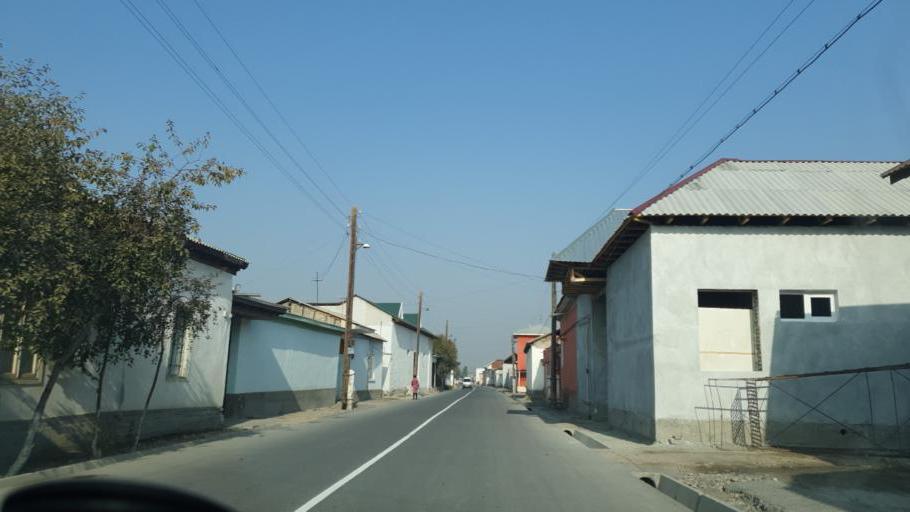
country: UZ
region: Fergana
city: Qo`qon
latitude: 40.5846
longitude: 70.9079
